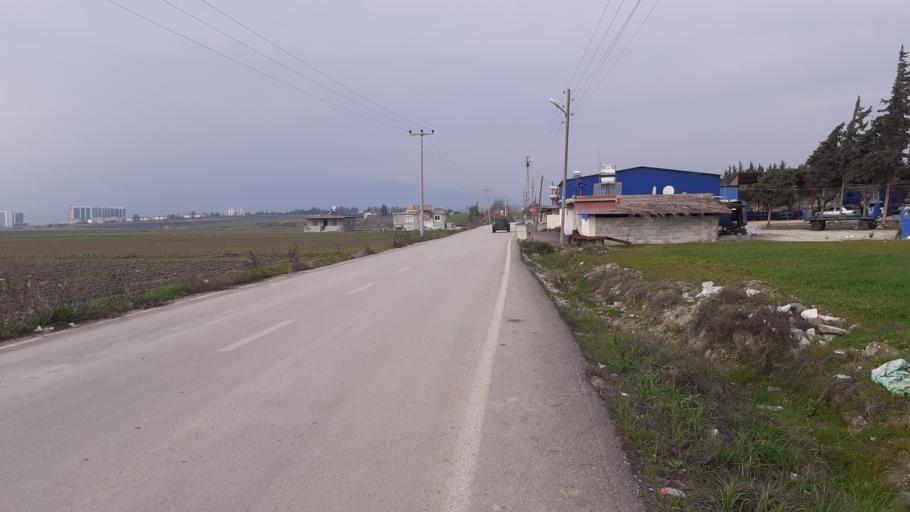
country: TR
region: Hatay
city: Kastal
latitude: 36.2628
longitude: 36.2424
